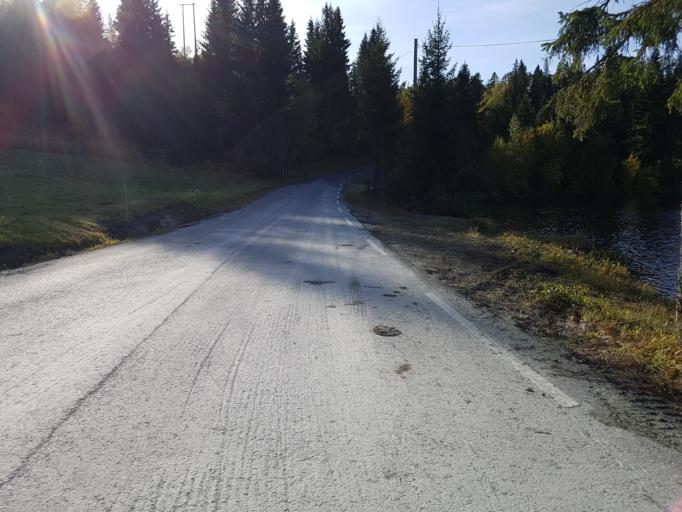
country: NO
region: Sor-Trondelag
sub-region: Klaebu
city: Klaebu
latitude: 63.3411
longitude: 10.5837
